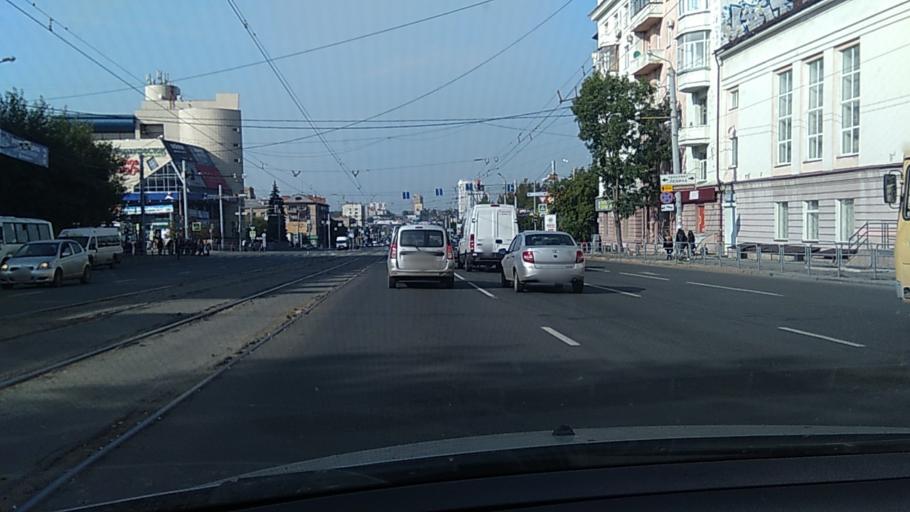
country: RU
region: Chelyabinsk
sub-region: Gorod Chelyabinsk
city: Chelyabinsk
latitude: 55.1589
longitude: 61.3892
